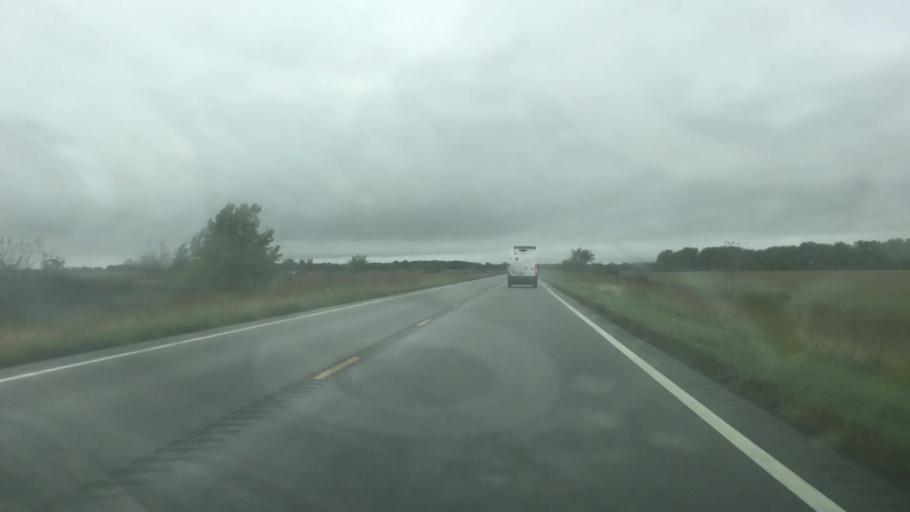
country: US
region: Kansas
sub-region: Anderson County
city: Garnett
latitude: 38.1363
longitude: -95.3325
